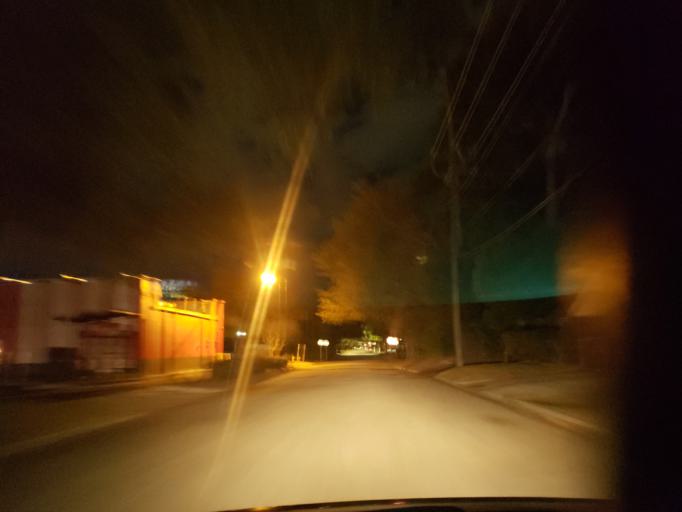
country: US
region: Georgia
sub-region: Chatham County
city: Thunderbolt
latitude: 32.0421
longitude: -81.0630
